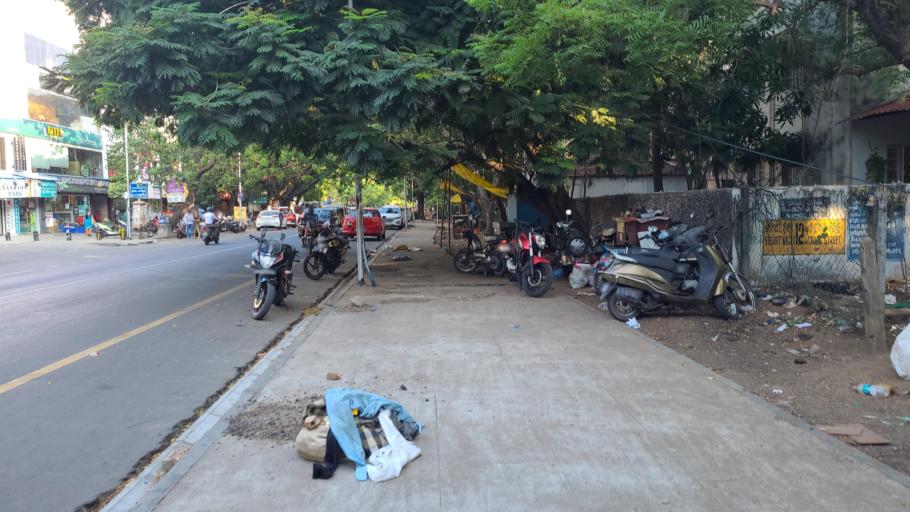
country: IN
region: Tamil Nadu
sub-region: Chennai
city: Gandhi Nagar
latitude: 12.9988
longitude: 80.2671
